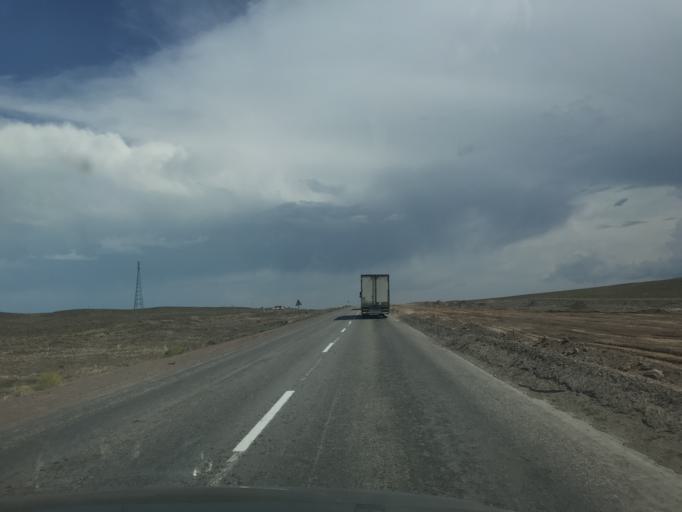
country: KZ
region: Zhambyl
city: Mynaral
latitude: 45.3312
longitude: 73.7260
